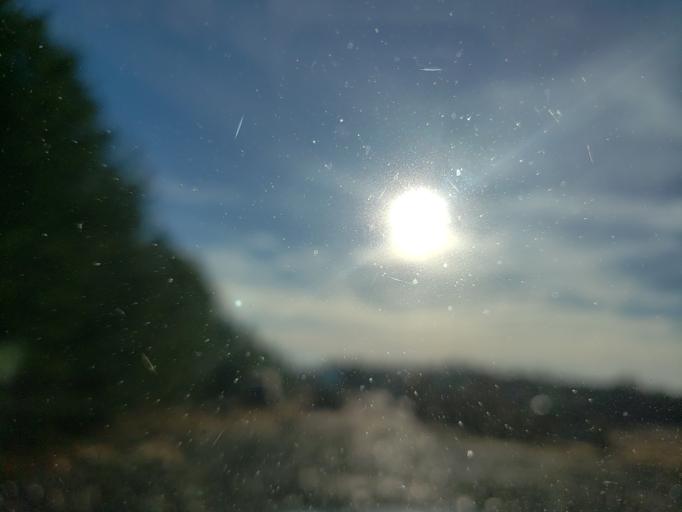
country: US
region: North Carolina
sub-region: Cleveland County
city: White Plains
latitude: 35.2017
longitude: -81.3939
